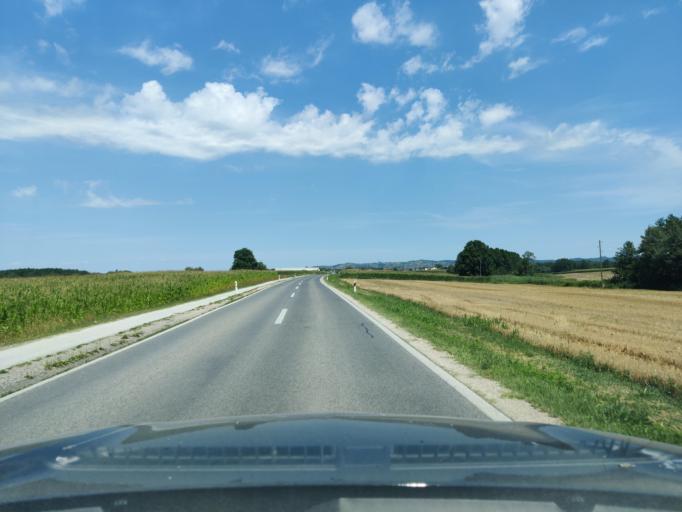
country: HR
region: Medimurska
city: Vratisinec
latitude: 46.4968
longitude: 16.4284
